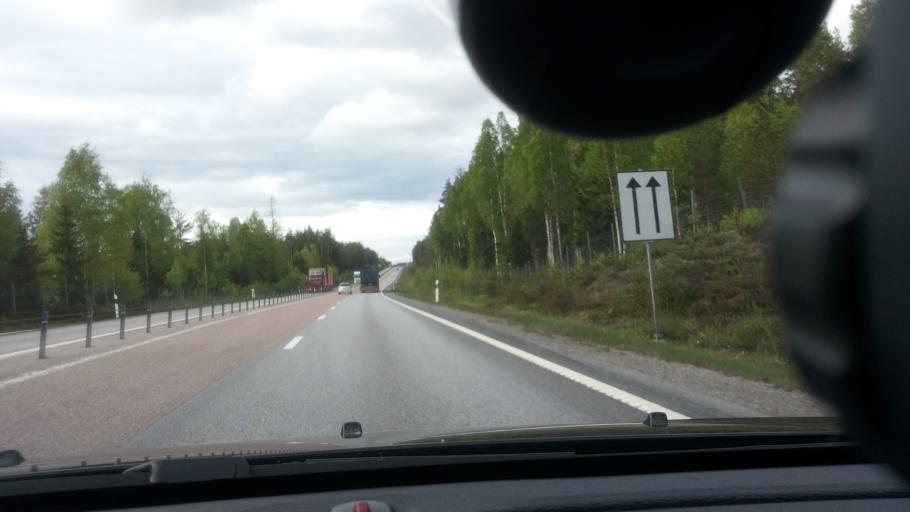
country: SE
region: Gaevleborg
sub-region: Soderhamns Kommun
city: Ljusne
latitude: 61.1855
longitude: 17.0458
